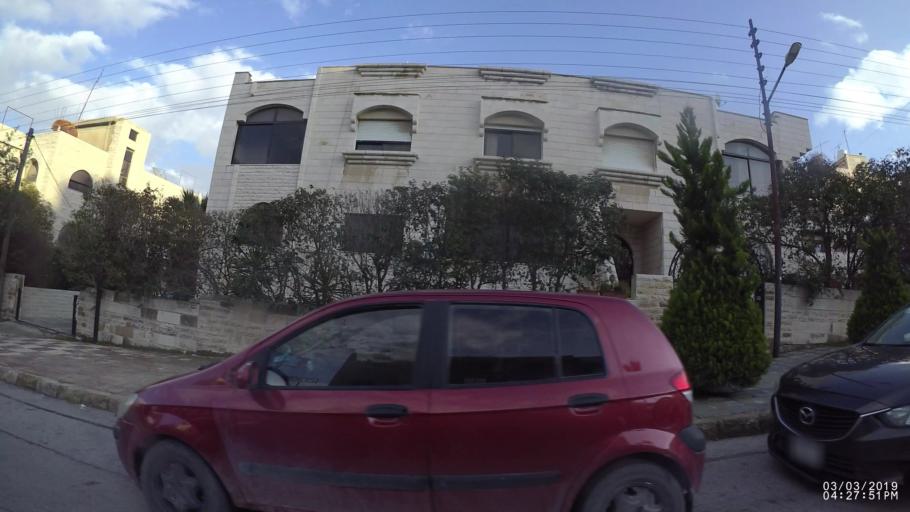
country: JO
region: Amman
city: Al Jubayhah
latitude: 31.9759
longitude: 35.8847
